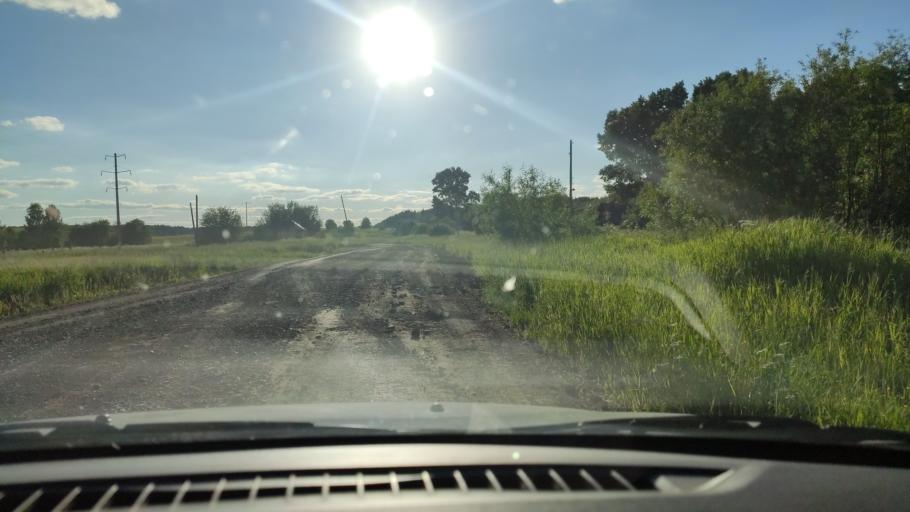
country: RU
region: Perm
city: Orda
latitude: 57.3011
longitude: 56.6193
